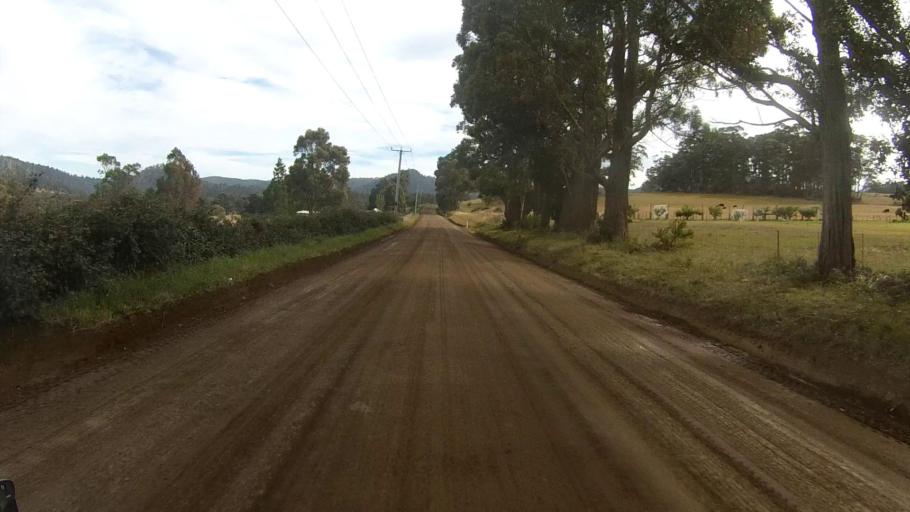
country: AU
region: Tasmania
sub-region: Sorell
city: Sorell
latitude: -42.7862
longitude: 147.8075
